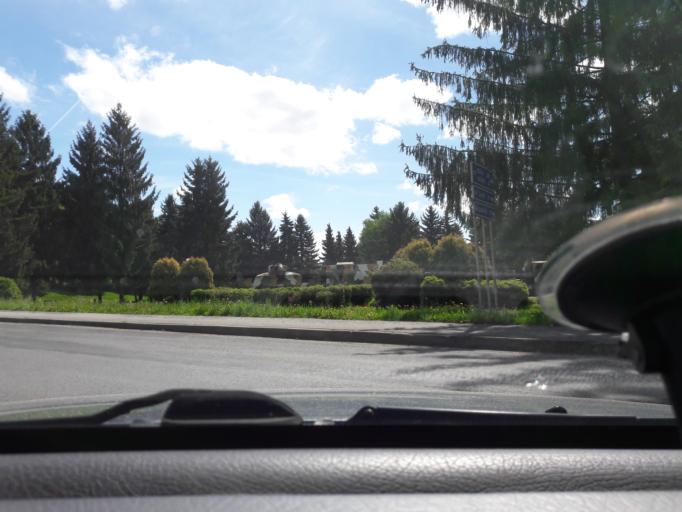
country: SK
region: Banskobystricky
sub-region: Okres Banska Bystrica
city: Zvolen
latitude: 48.5729
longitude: 19.1244
